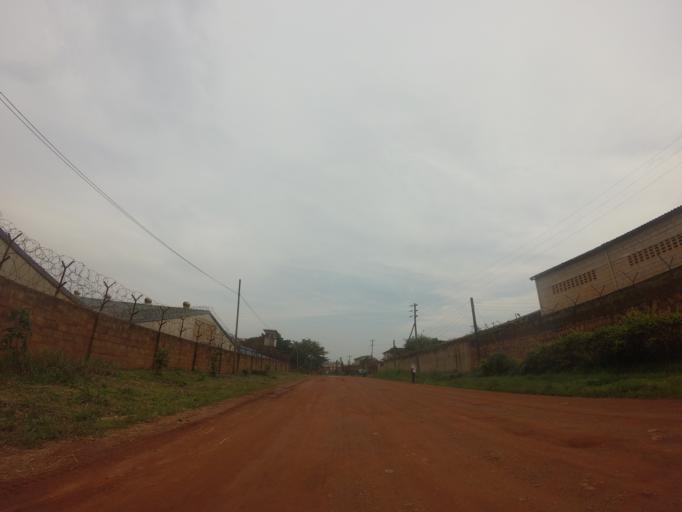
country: UG
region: Central Region
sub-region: Wakiso District
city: Kireka
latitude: 0.3421
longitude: 32.6226
